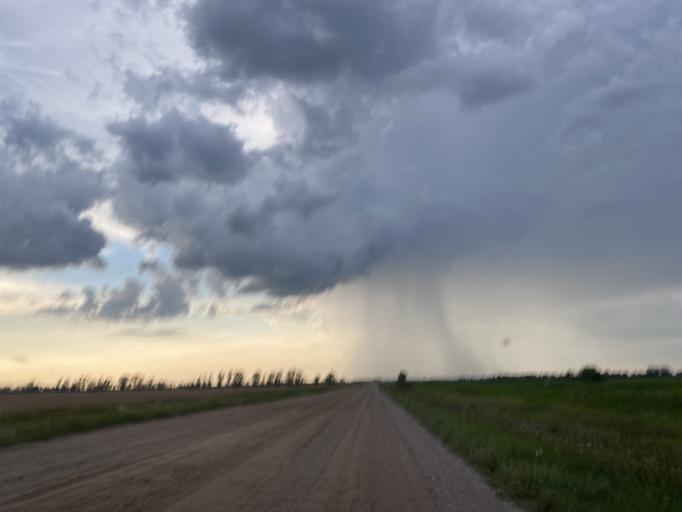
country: BY
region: Brest
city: Tsyelyakhany
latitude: 52.4636
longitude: 25.5715
